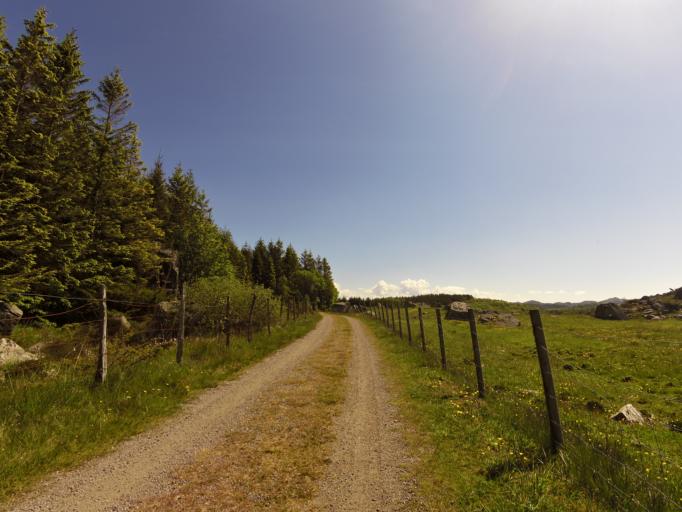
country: NO
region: Rogaland
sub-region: Eigersund
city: Egersund
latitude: 58.5028
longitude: 5.9005
